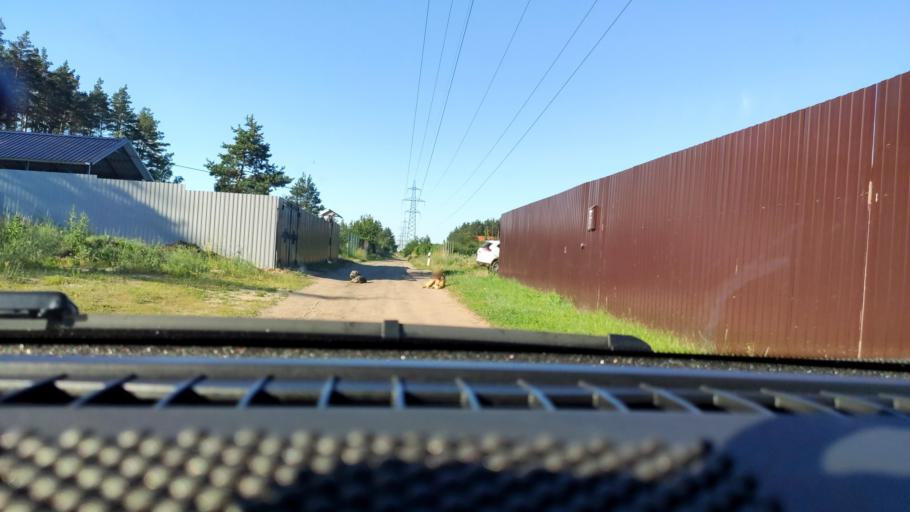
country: RU
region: Voronezj
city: Volya
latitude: 51.7435
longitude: 39.4609
